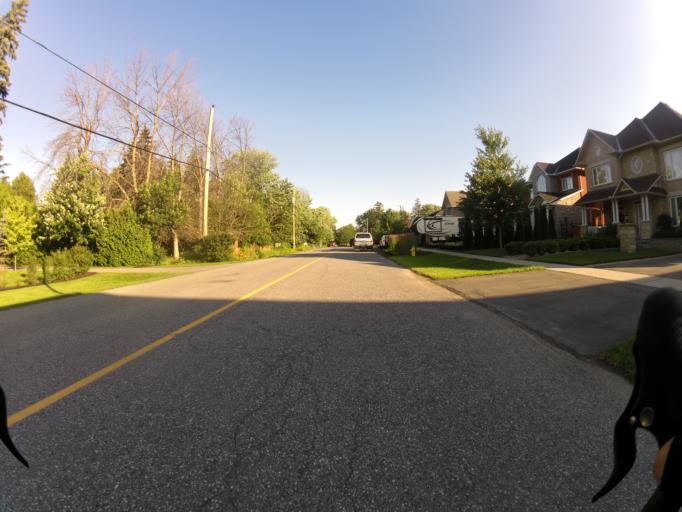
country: CA
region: Ontario
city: Ottawa
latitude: 45.2882
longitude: -75.7001
